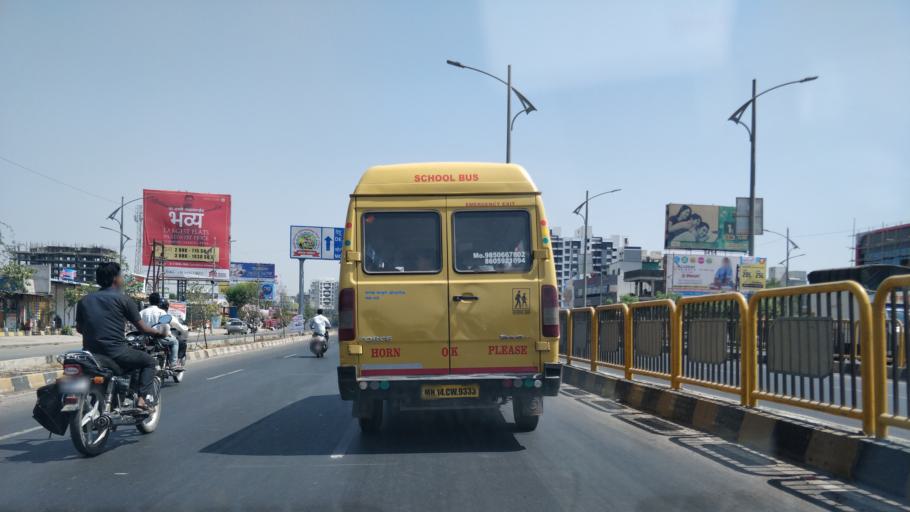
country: IN
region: Maharashtra
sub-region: Pune Division
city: Alandi
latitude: 18.6596
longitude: 73.8862
